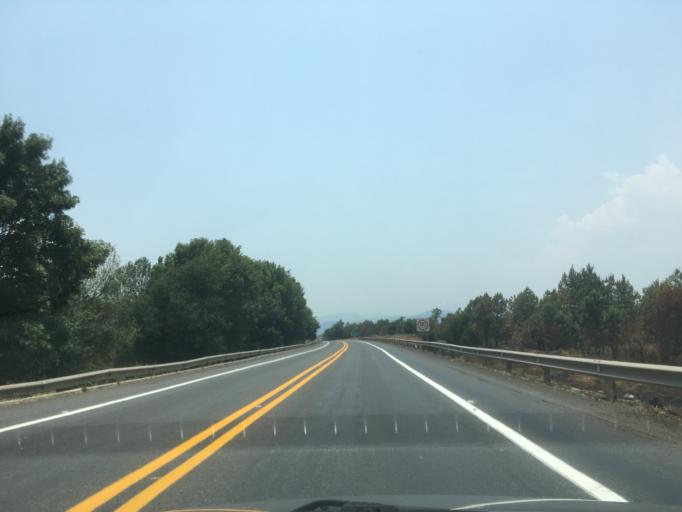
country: MX
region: Michoacan
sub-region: Patzcuaro
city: Santa Ana Chapitiro
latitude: 19.5068
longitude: -101.6658
